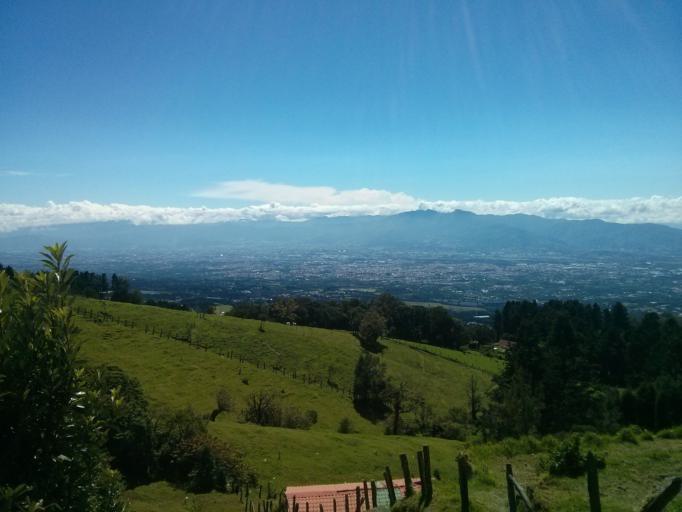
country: CR
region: Heredia
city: Santo Domingo
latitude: 10.1120
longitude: -84.1223
